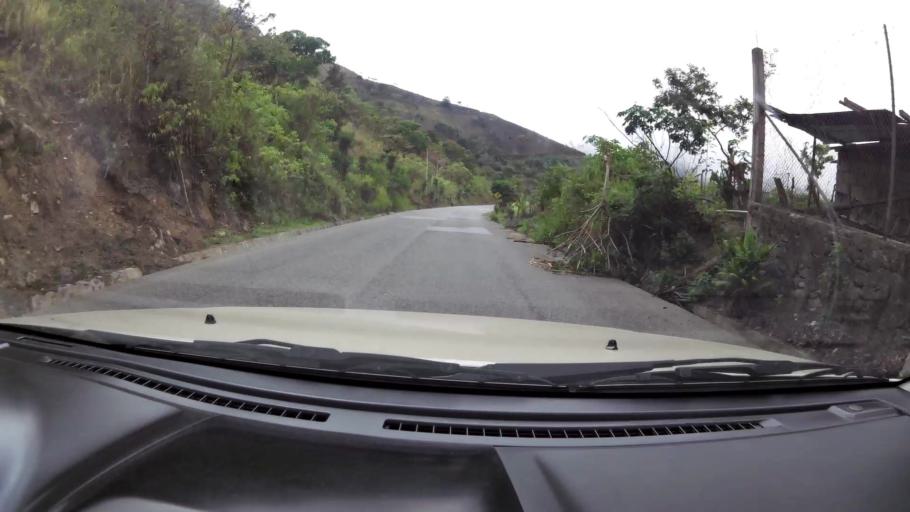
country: EC
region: El Oro
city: Pasaje
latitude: -3.3029
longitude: -79.5277
